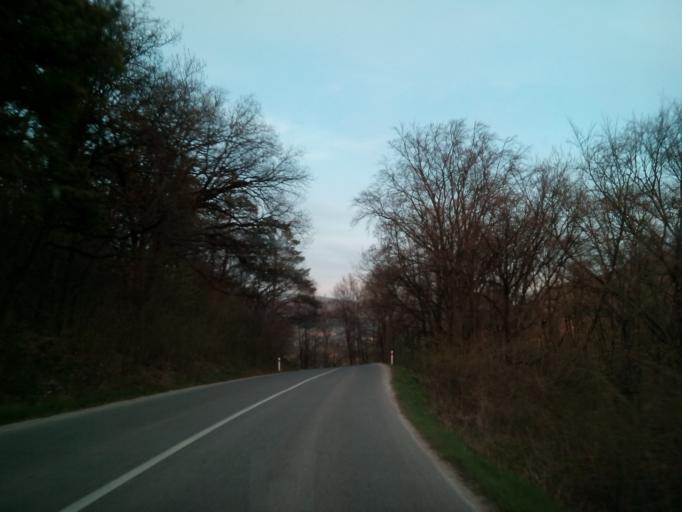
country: SK
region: Kosicky
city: Roznava
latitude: 48.6638
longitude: 20.3905
